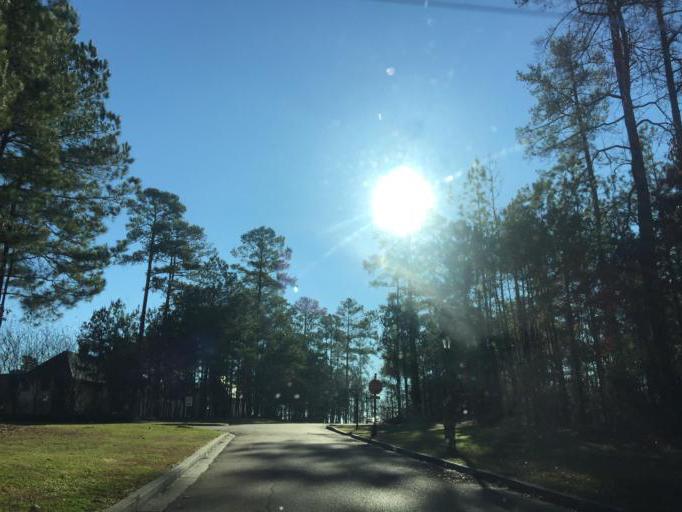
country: US
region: Mississippi
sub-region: Madison County
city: Madison
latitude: 32.4592
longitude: -90.0585
